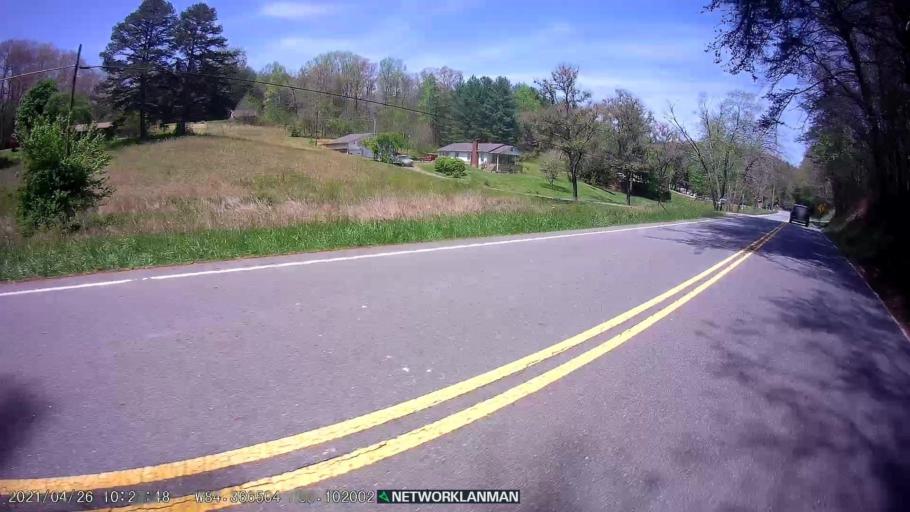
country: US
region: Georgia
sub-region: Fannin County
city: McCaysville
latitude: 35.1022
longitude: -84.3665
